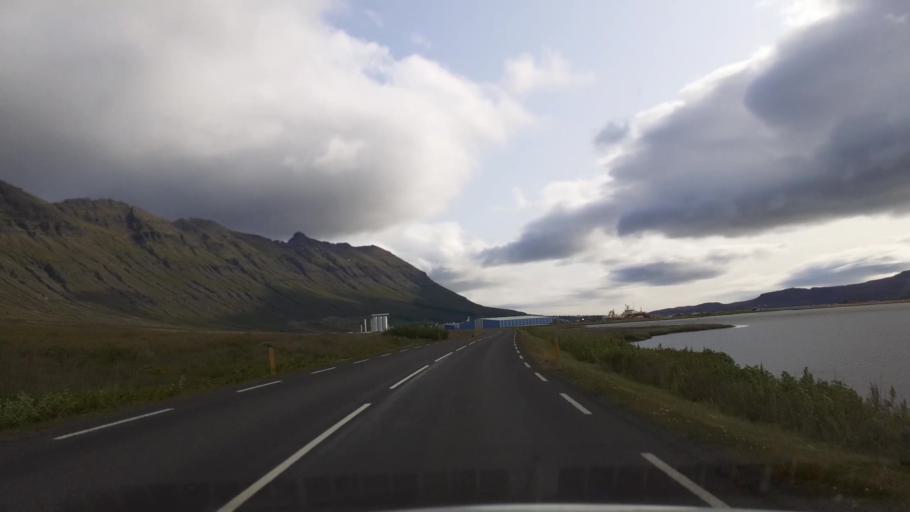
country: IS
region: East
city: Neskaupstadur
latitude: 65.1324
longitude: -13.7588
